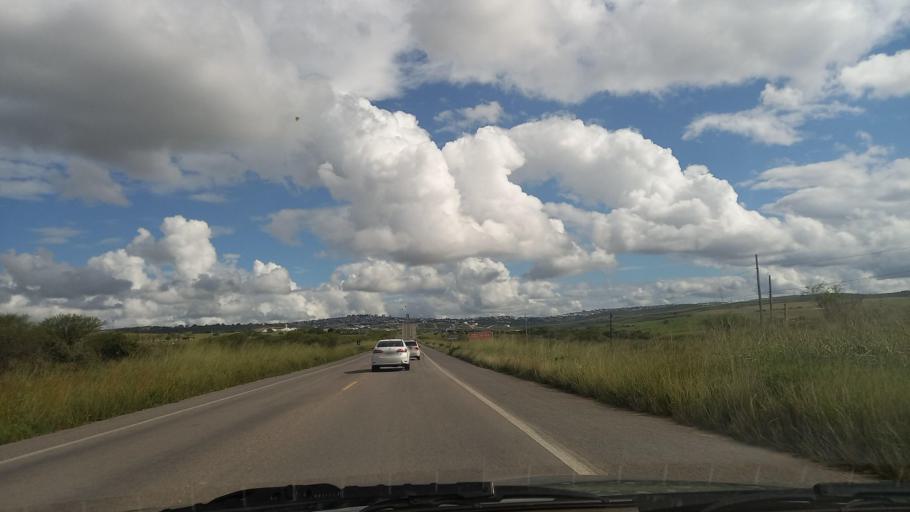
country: BR
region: Pernambuco
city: Garanhuns
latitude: -8.8357
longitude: -36.4552
